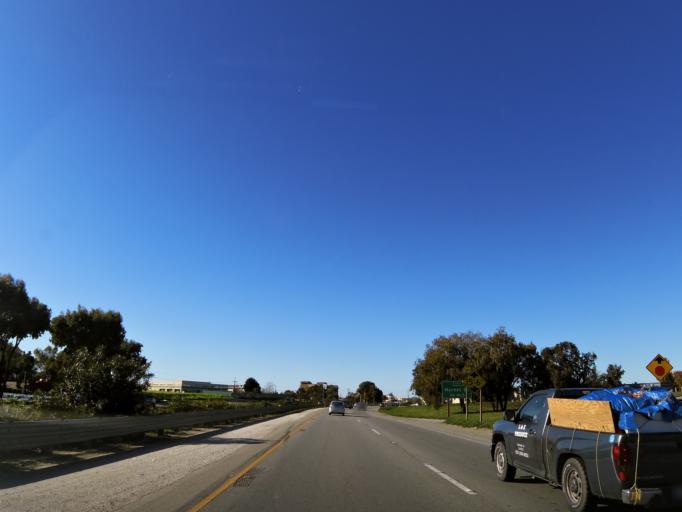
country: US
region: California
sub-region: Monterey County
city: Salinas
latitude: 36.6690
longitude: -121.6352
